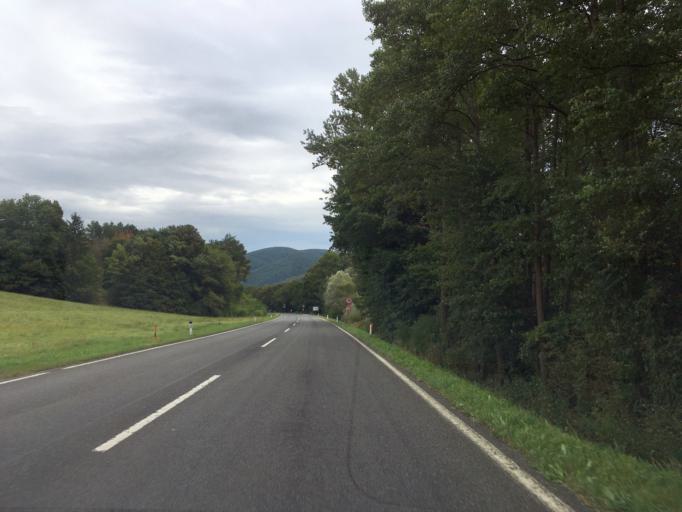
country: AT
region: Lower Austria
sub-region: Politischer Bezirk Modling
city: Gaaden
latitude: 48.0533
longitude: 16.1915
